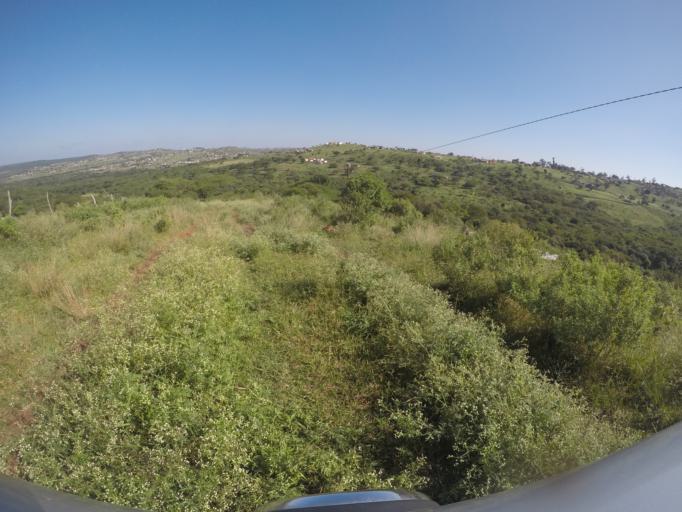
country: ZA
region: KwaZulu-Natal
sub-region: uThungulu District Municipality
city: Empangeni
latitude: -28.5765
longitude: 31.7324
